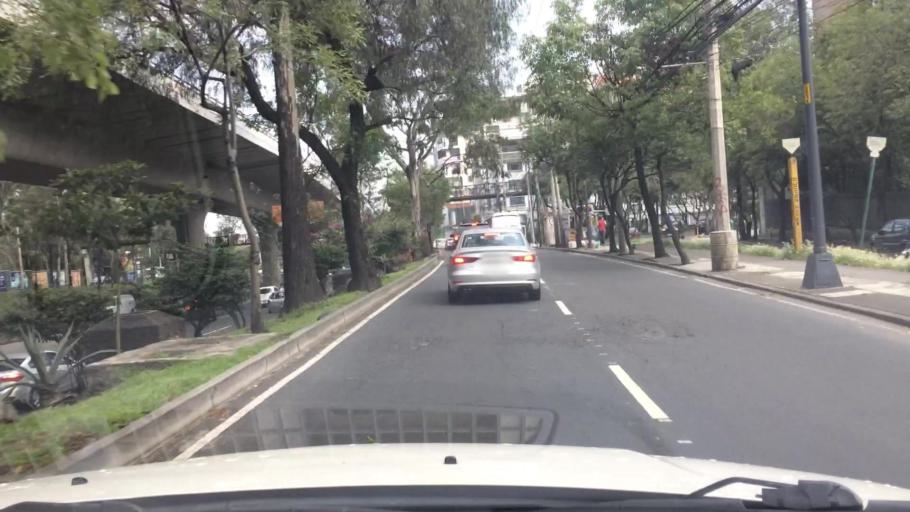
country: MX
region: Mexico City
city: Magdalena Contreras
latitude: 19.3032
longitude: -99.1988
